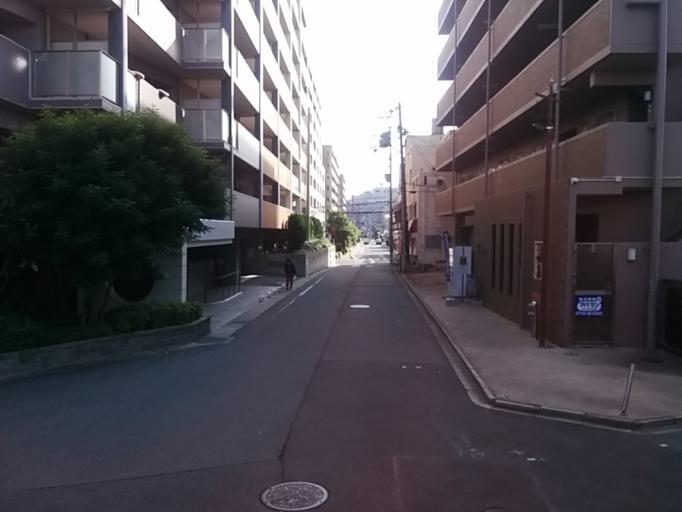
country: JP
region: Nara
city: Nara-shi
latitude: 34.6956
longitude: 135.7805
